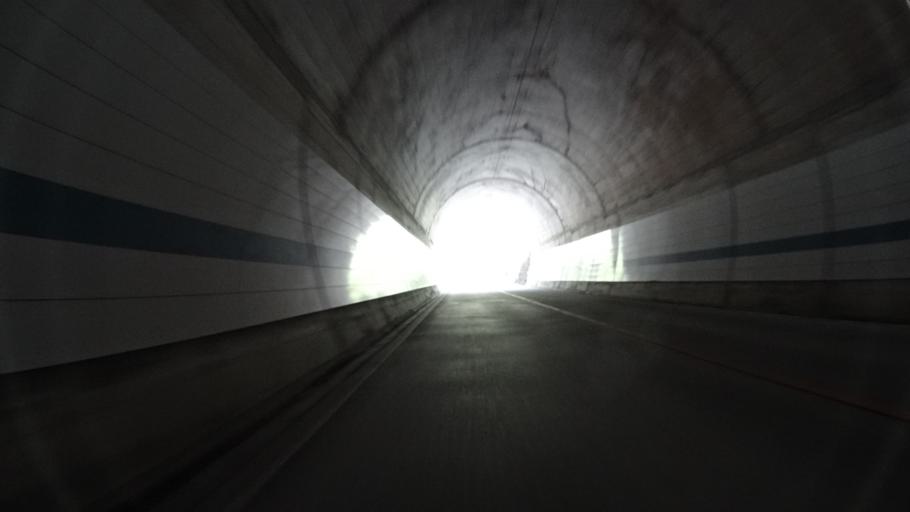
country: JP
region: Yamanashi
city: Kofu-shi
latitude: 35.7240
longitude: 138.5569
